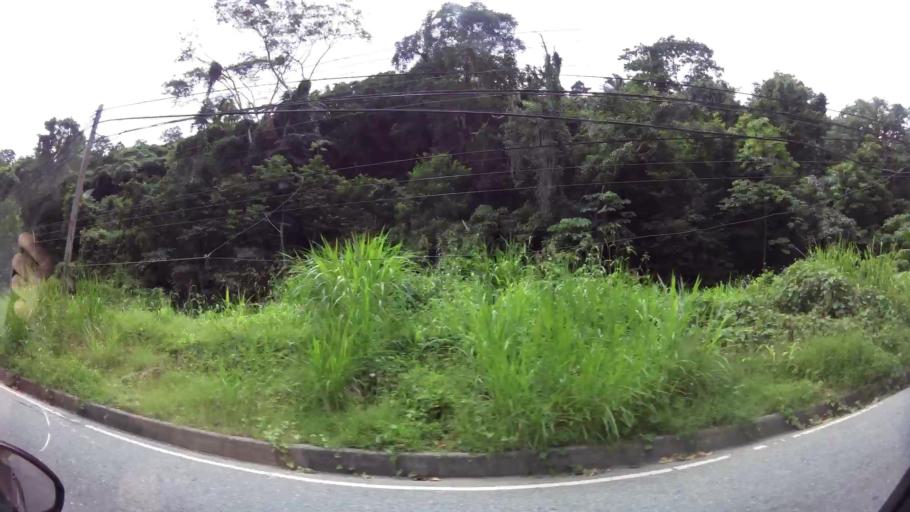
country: TT
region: Diego Martin
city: Petit Valley
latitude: 10.7145
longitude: -61.5183
